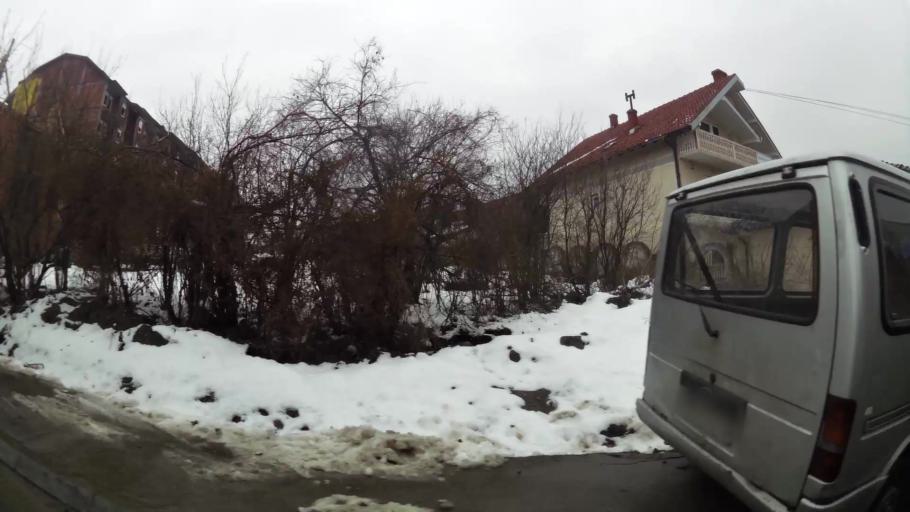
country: RS
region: Central Serbia
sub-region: Belgrade
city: Zvezdara
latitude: 44.7651
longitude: 20.5153
